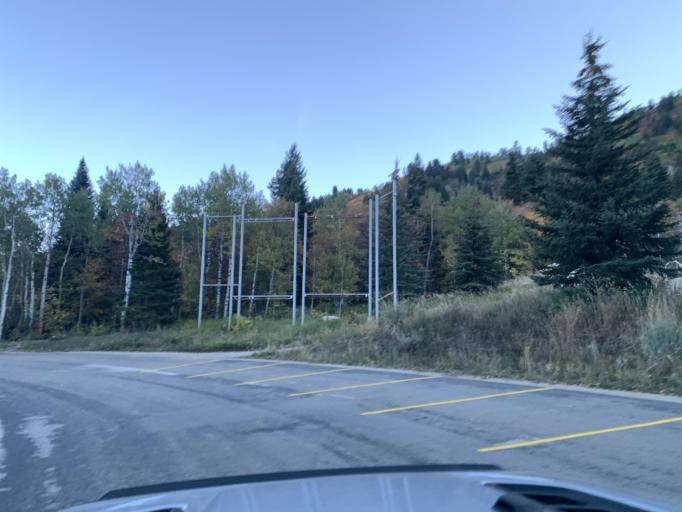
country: US
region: Utah
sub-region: Weber County
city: Uintah
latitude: 41.2172
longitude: -111.8634
